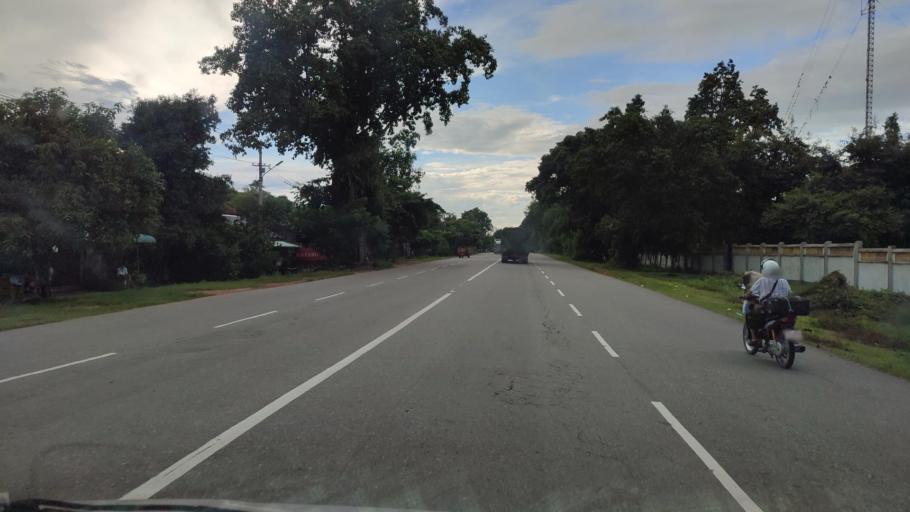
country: MM
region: Bago
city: Taungoo
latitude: 19.0161
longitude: 96.3842
